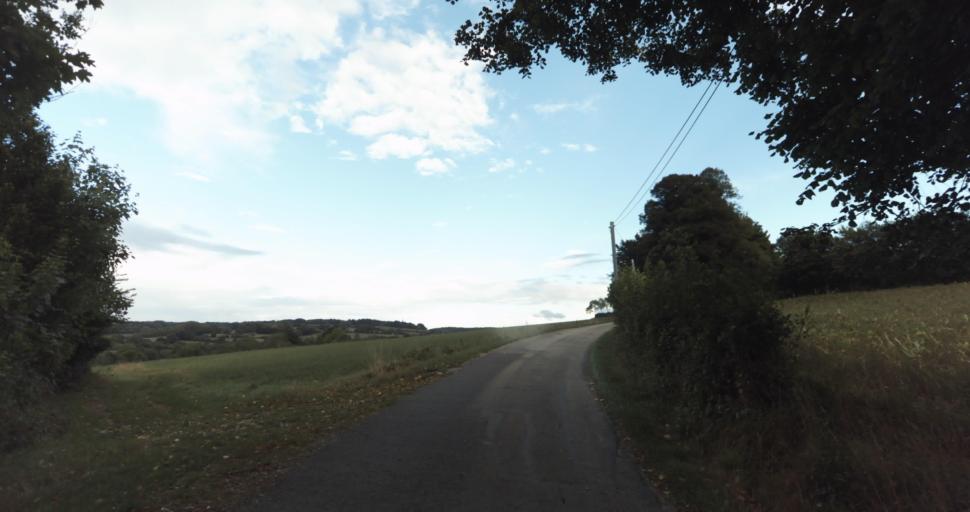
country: FR
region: Lower Normandy
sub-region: Departement de l'Orne
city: Gace
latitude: 48.7724
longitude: 0.3501
